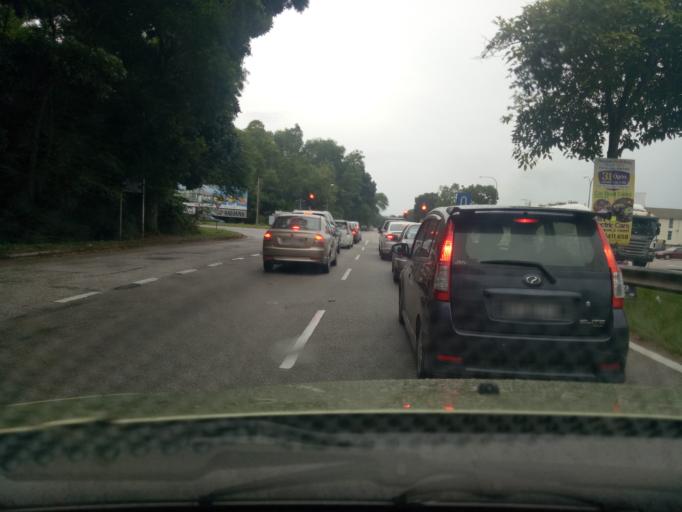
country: MY
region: Kedah
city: Sungai Petani
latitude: 5.6674
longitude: 100.5278
